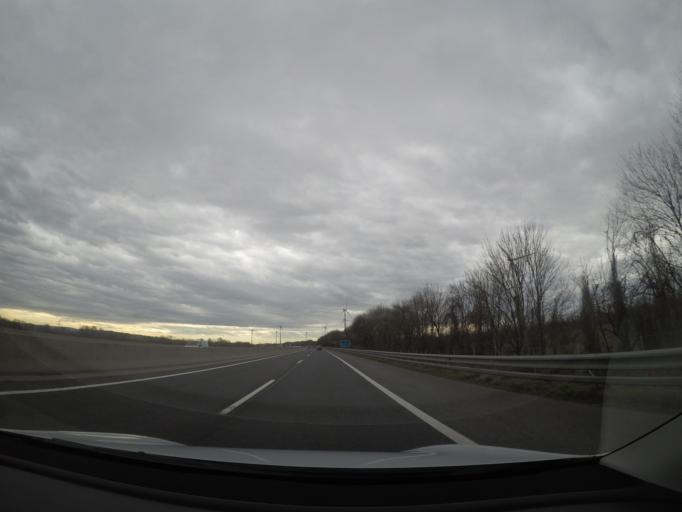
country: AT
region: Lower Austria
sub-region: Politischer Bezirk Baden
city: Ebreichsdorf
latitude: 47.9590
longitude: 16.3661
